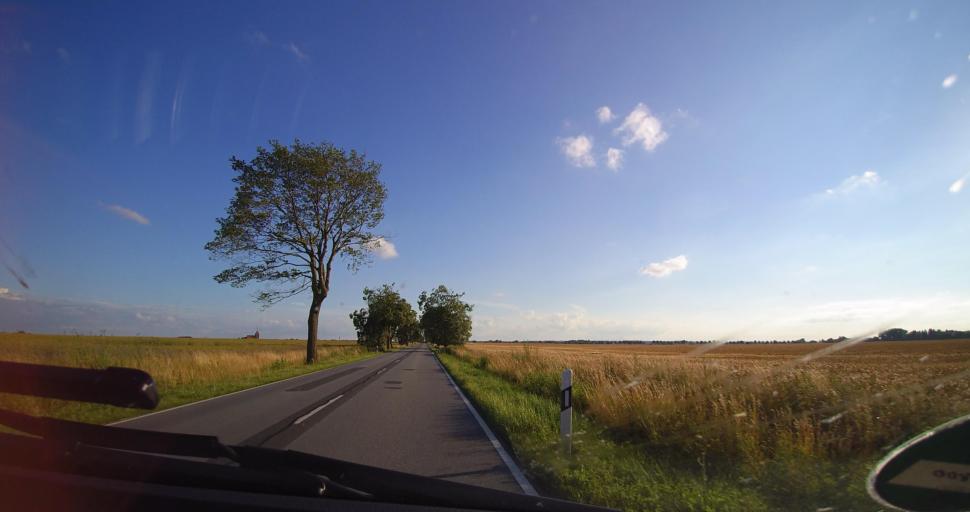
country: DE
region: Mecklenburg-Vorpommern
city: Tribsees
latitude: 54.1106
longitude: 12.7656
